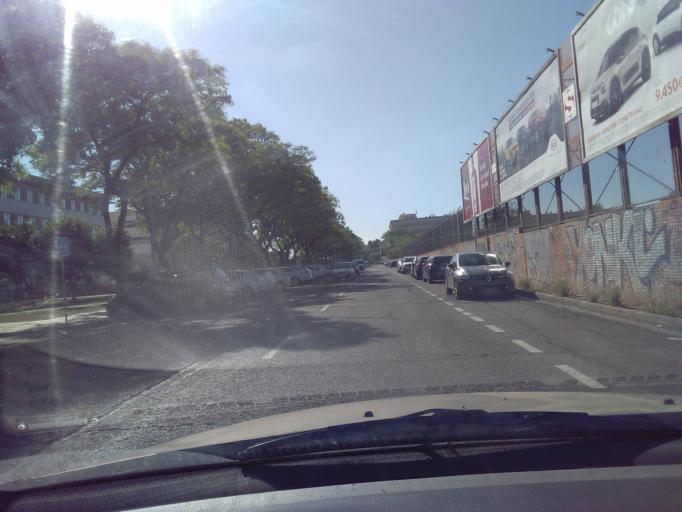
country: ES
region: Andalusia
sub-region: Provincia de Sevilla
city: Sevilla
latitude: 37.4077
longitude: -5.9311
